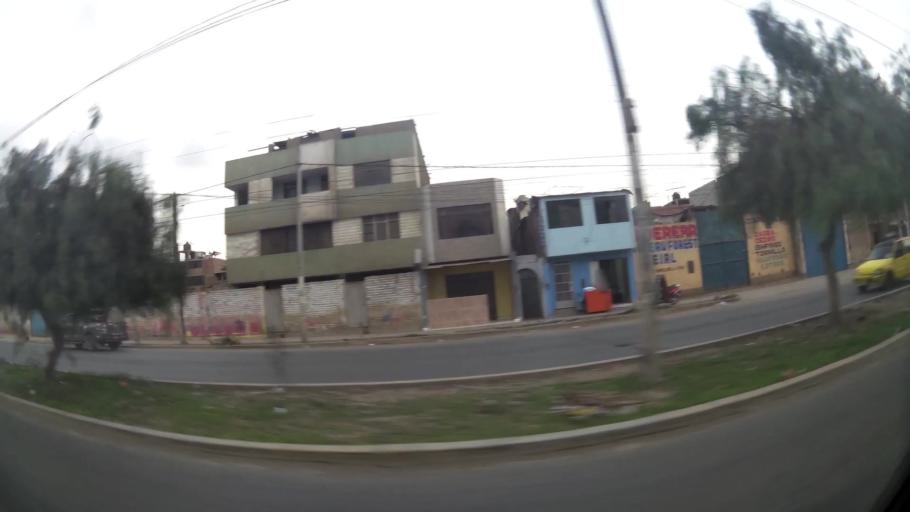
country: PE
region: La Libertad
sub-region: Provincia de Trujillo
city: El Porvenir
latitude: -8.0919
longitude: -79.0176
